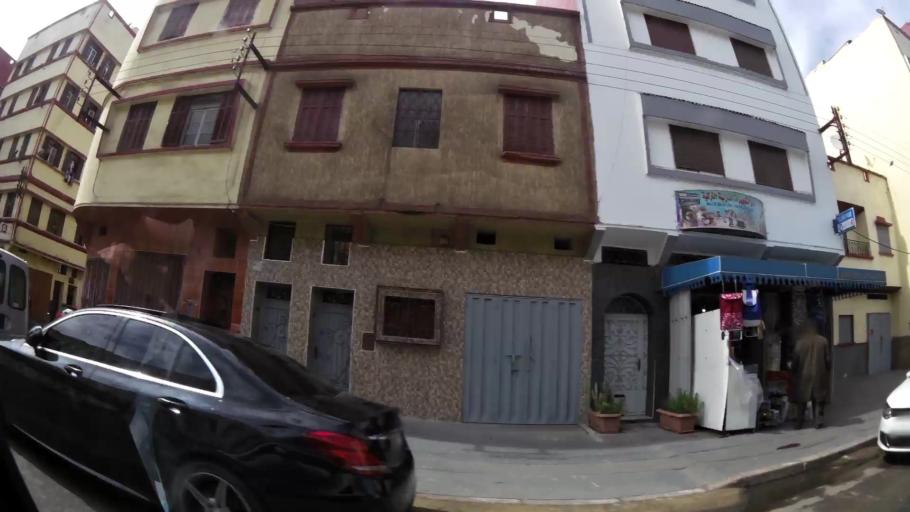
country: MA
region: Grand Casablanca
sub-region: Casablanca
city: Casablanca
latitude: 33.5438
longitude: -7.5685
